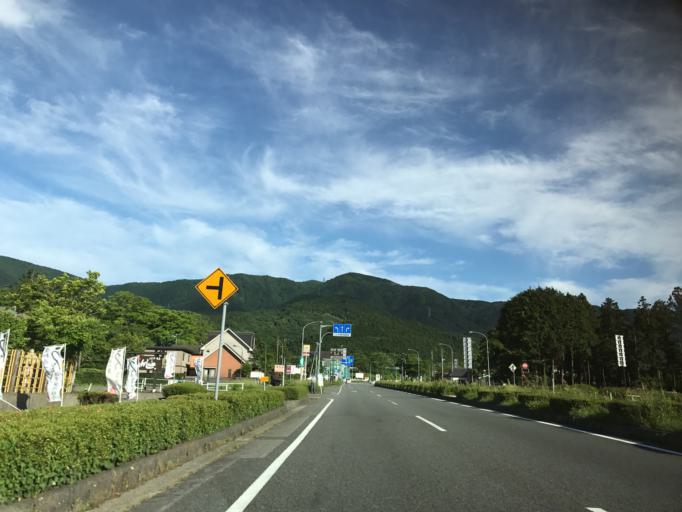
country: JP
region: Shizuoka
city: Gotemba
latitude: 35.2948
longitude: 138.9543
